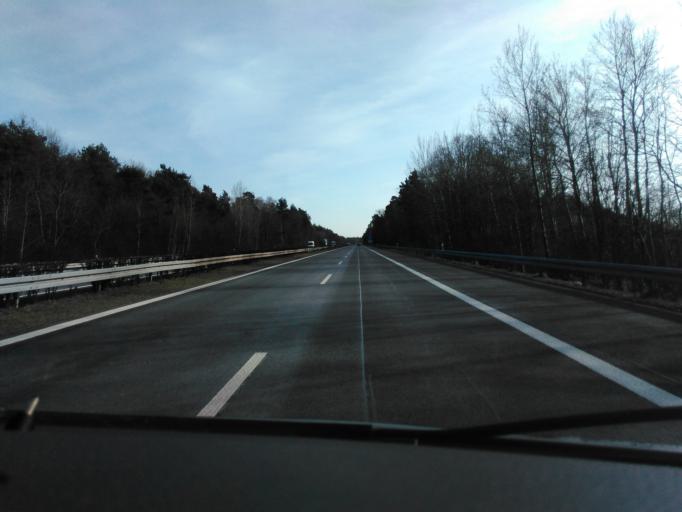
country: DE
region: Brandenburg
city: Bronkow
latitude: 51.6195
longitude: 13.9470
